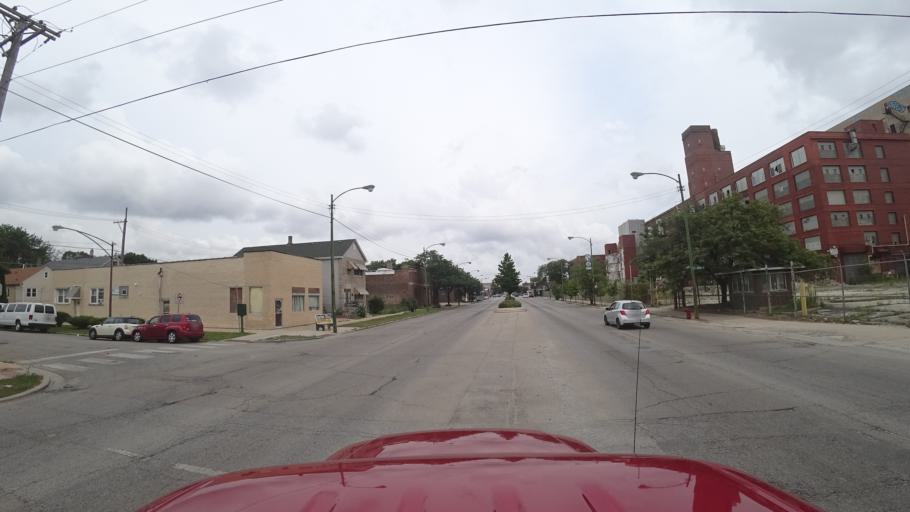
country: US
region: Illinois
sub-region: Cook County
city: Chicago
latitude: 41.8287
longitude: -87.6655
